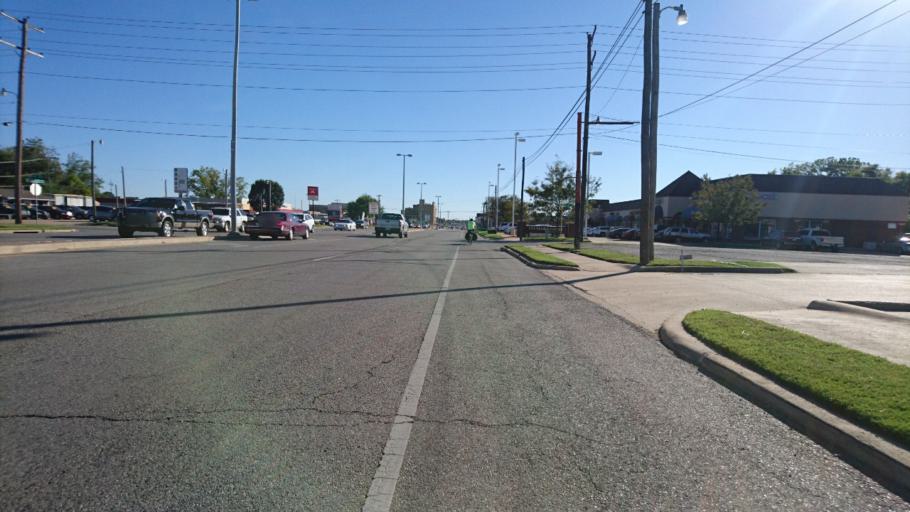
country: US
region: Oklahoma
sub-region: Rogers County
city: Claremore
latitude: 36.3167
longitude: -95.6136
